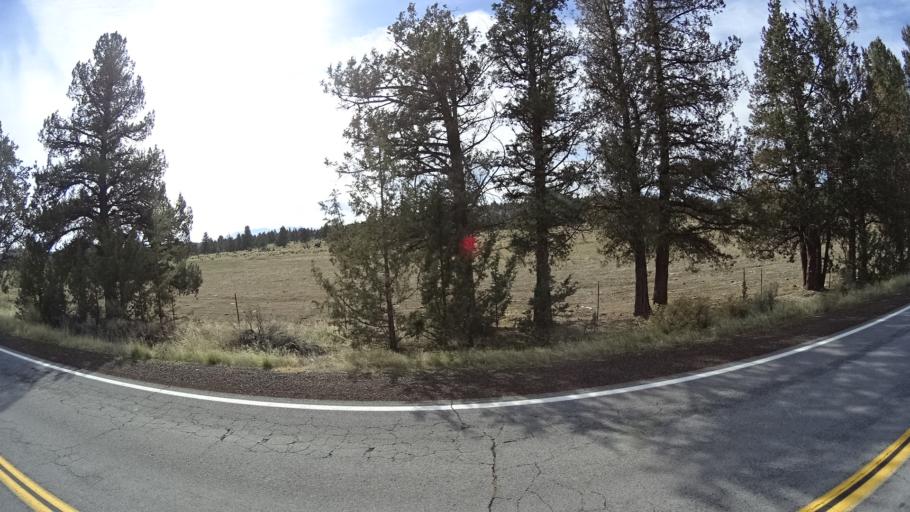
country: US
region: California
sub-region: Siskiyou County
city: Weed
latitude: 41.5542
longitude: -122.3833
